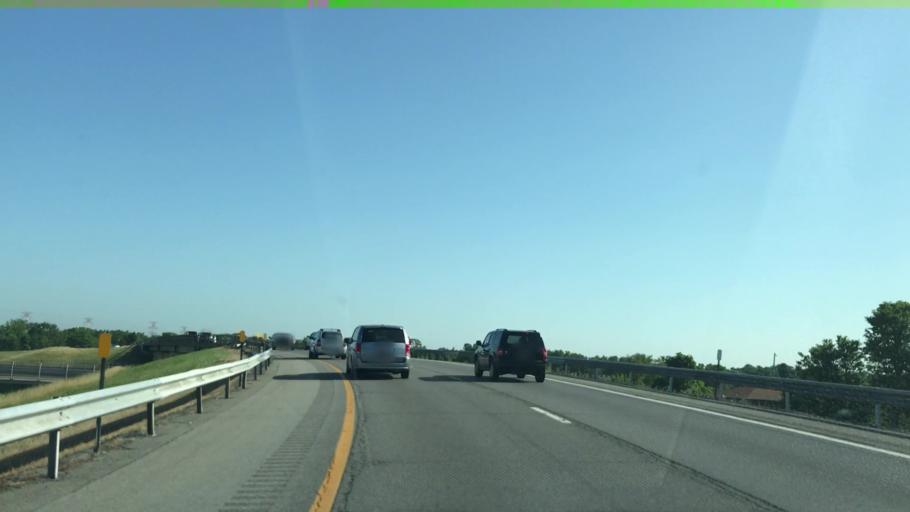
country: US
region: New York
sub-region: Erie County
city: Williamsville
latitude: 42.9485
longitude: -78.7629
